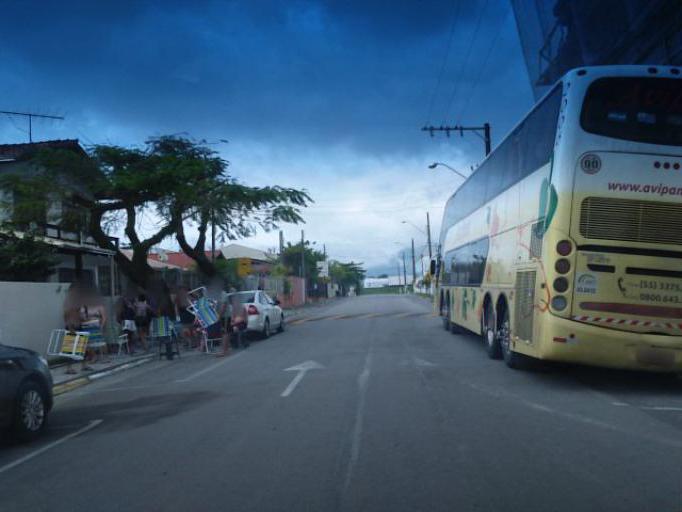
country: BR
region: Santa Catarina
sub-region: Itapema
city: Itapema
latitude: -27.1287
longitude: -48.6080
